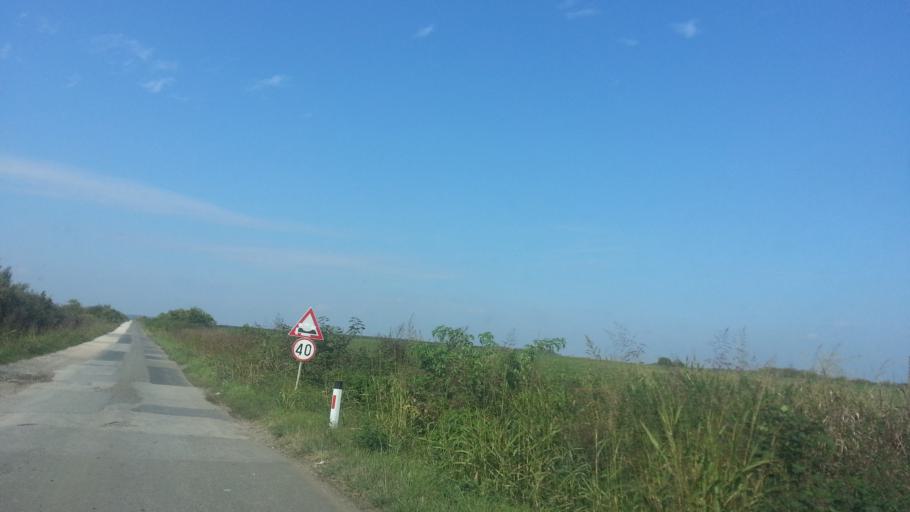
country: RS
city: Surduk
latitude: 45.0998
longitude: 20.2899
